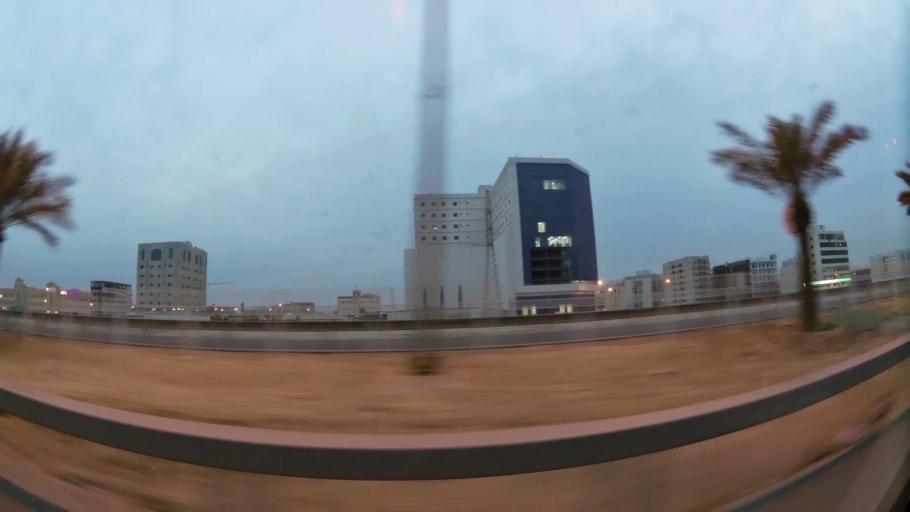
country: BH
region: Northern
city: Ar Rifa'
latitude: 26.1549
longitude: 50.5701
